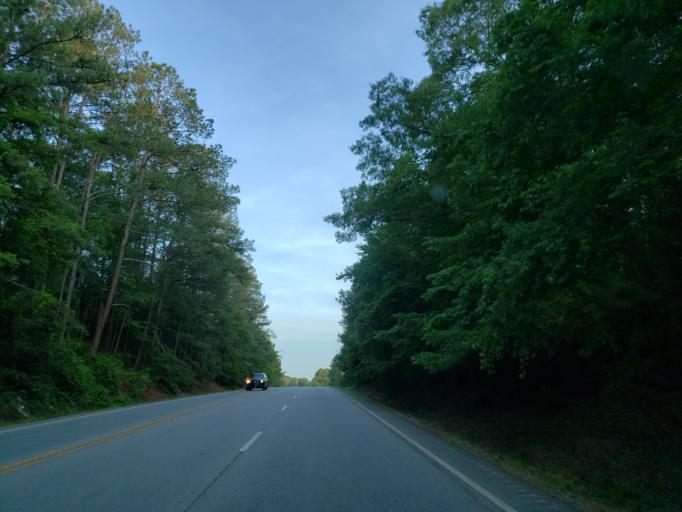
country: US
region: Georgia
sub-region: Coweta County
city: Newnan
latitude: 33.4632
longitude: -84.8922
